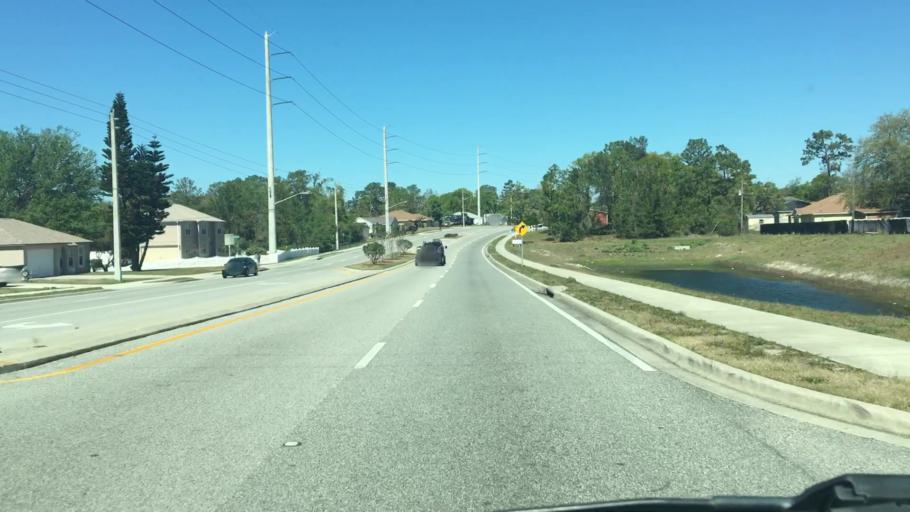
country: US
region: Florida
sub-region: Volusia County
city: Deltona
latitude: 28.9079
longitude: -81.1784
